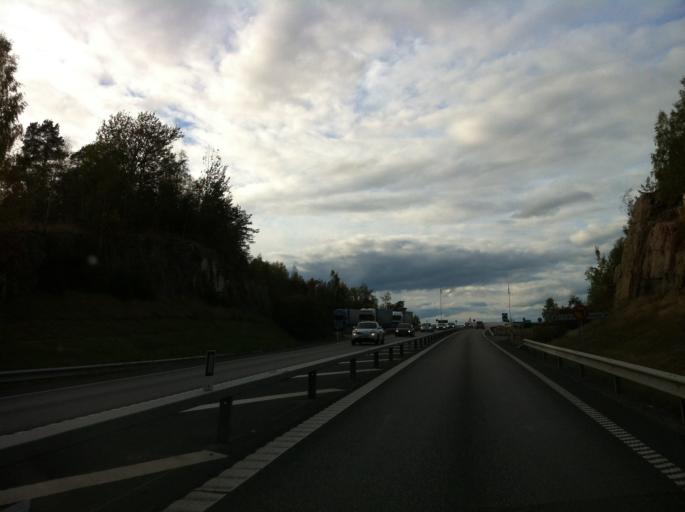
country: SE
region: OErebro
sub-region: Askersunds Kommun
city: Askersund
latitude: 58.8071
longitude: 14.9517
